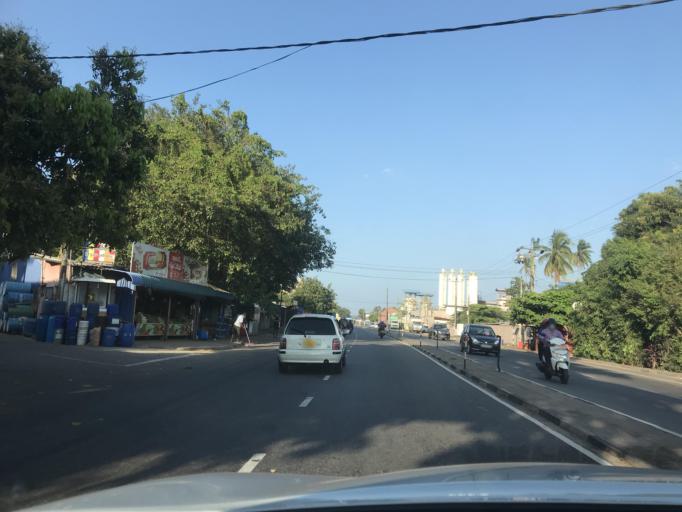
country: LK
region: Western
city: Ja Ela
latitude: 7.0915
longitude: 79.9021
